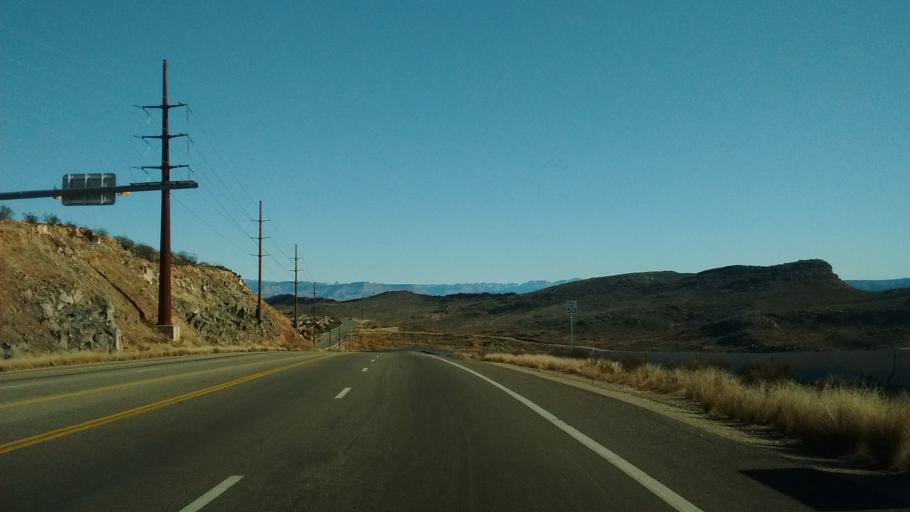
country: US
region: Utah
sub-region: Washington County
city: Washington
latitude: 37.1385
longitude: -113.4681
